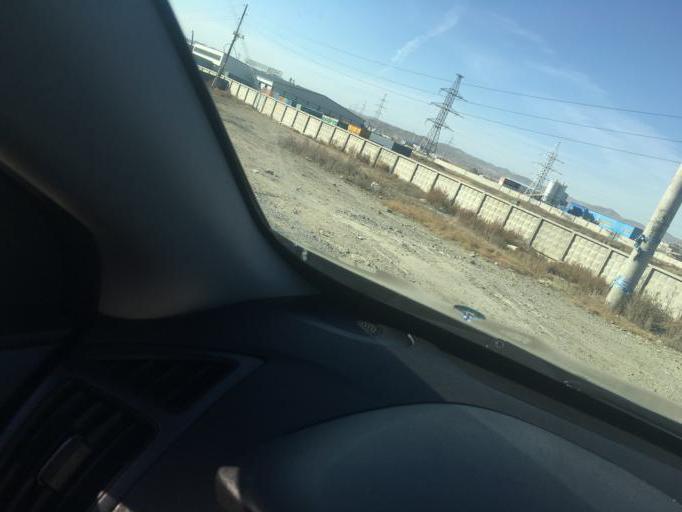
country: MN
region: Ulaanbaatar
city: Ulaanbaatar
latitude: 47.8883
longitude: 106.7849
